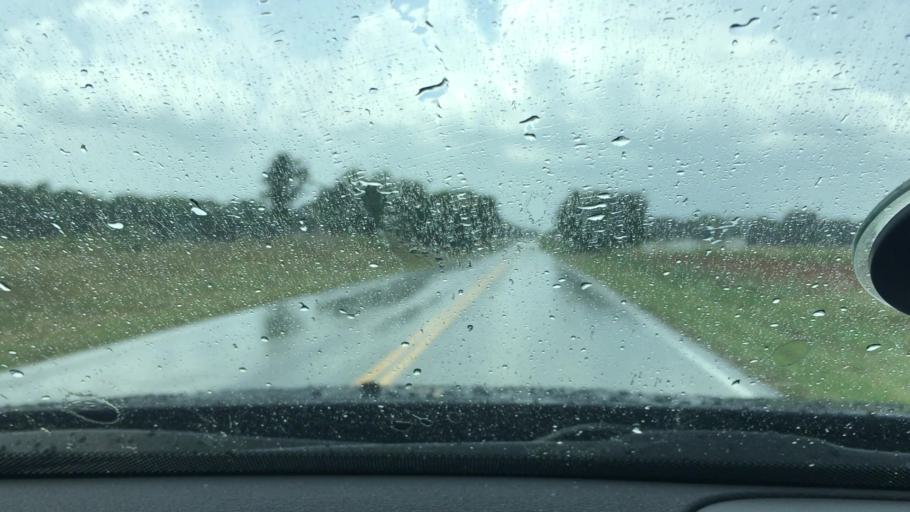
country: US
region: Oklahoma
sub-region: Johnston County
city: Tishomingo
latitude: 34.1813
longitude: -96.7164
